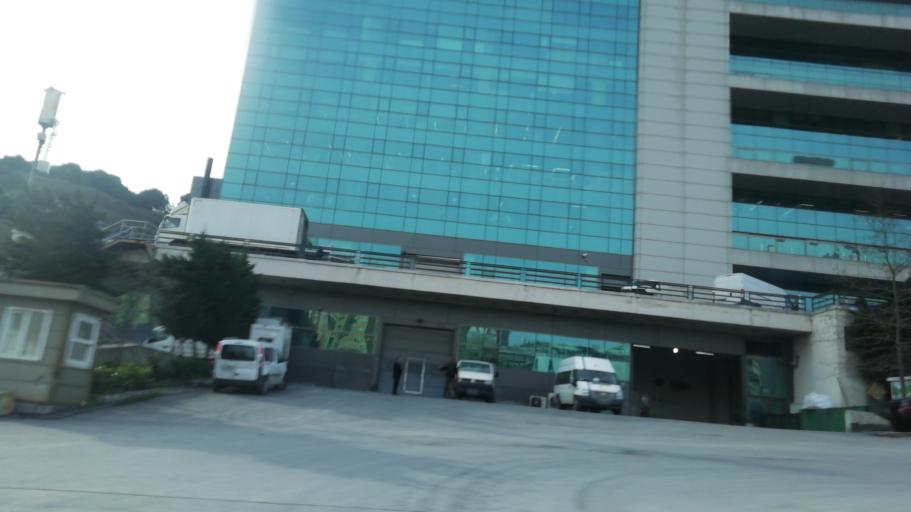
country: TR
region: Istanbul
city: Basaksehir
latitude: 41.0949
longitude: 28.8018
